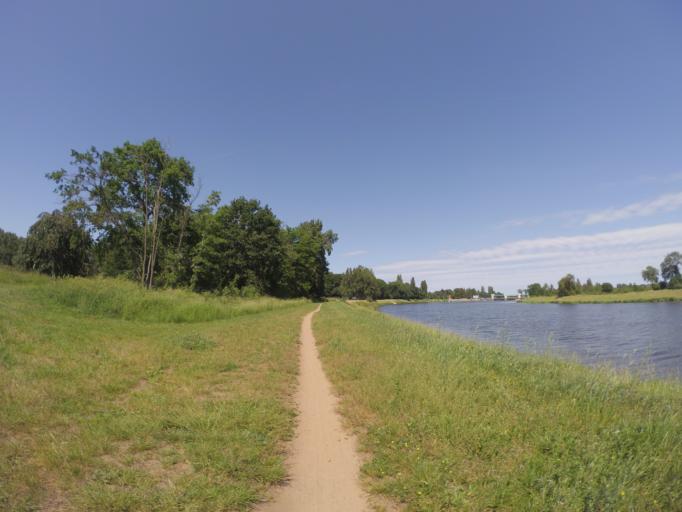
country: CZ
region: Central Bohemia
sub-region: Okres Nymburk
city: Sadska
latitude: 50.1664
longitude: 14.9772
